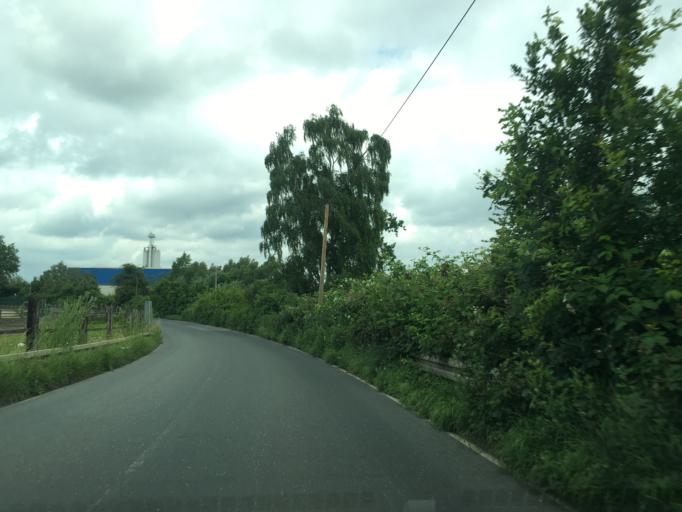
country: DE
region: North Rhine-Westphalia
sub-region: Regierungsbezirk Munster
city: Gelsenkirchen
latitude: 51.5409
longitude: 7.1259
